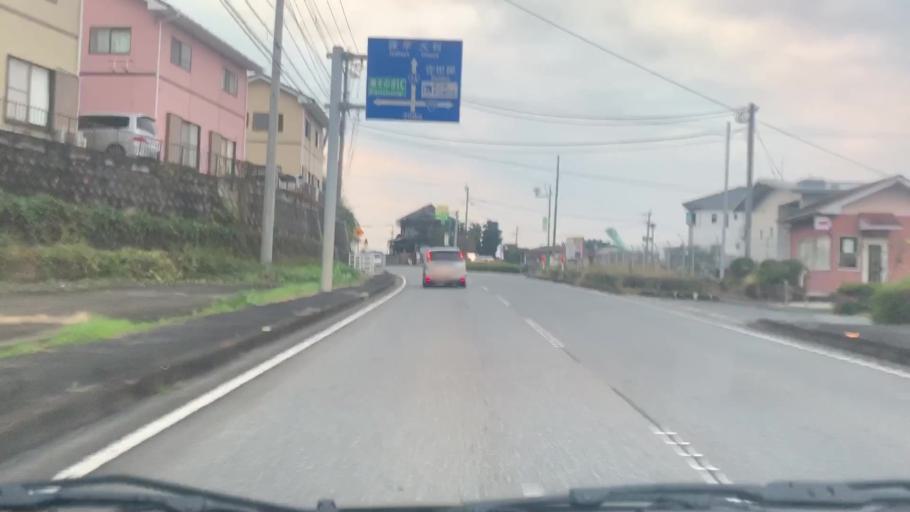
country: JP
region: Saga Prefecture
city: Ureshinomachi-shimojuku
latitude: 33.0382
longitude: 129.9219
